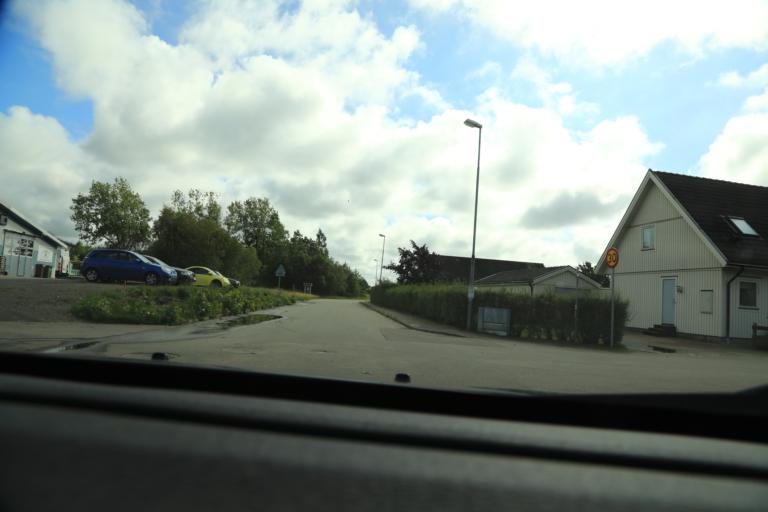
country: SE
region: Halland
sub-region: Varbergs Kommun
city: Traslovslage
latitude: 57.0790
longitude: 12.2775
